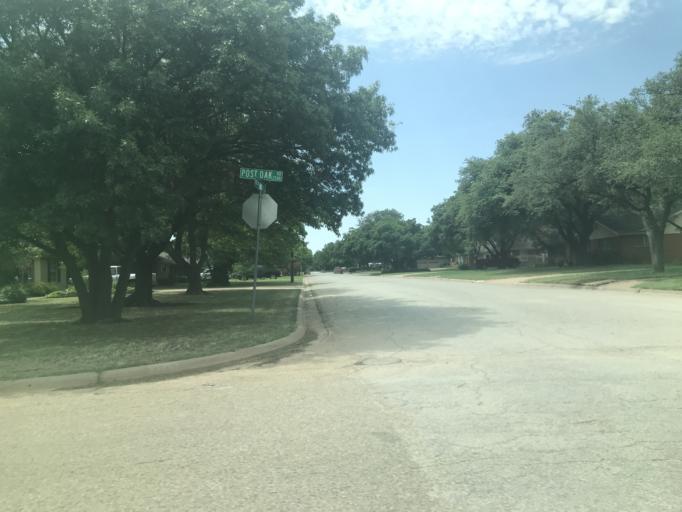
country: US
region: Texas
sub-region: Taylor County
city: Abilene
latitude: 32.4190
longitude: -99.7787
